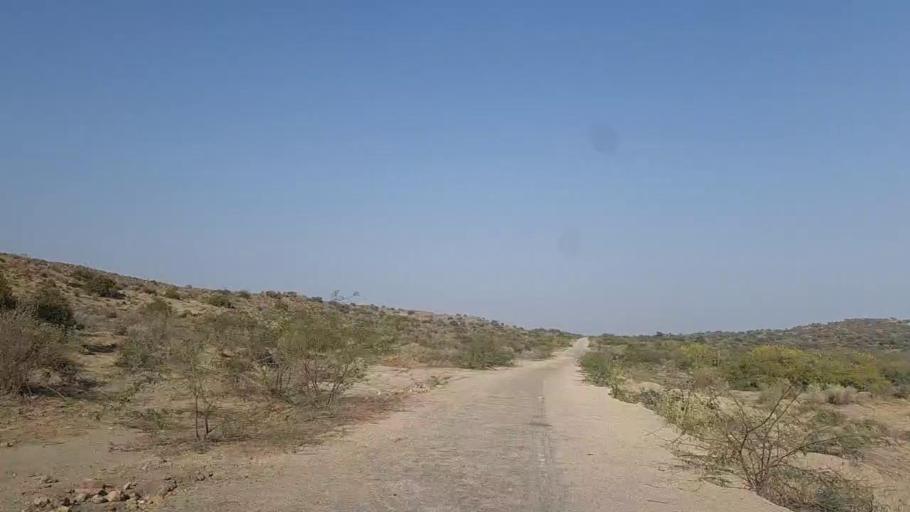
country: PK
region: Sindh
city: Naukot
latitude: 24.5995
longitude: 69.3219
